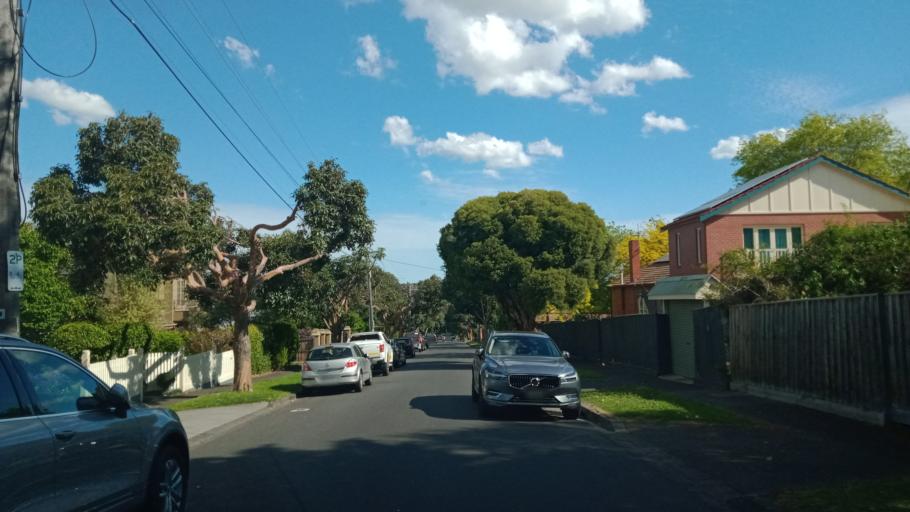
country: AU
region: Victoria
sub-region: Stonnington
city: Glen Iris
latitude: -37.8473
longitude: 145.0565
